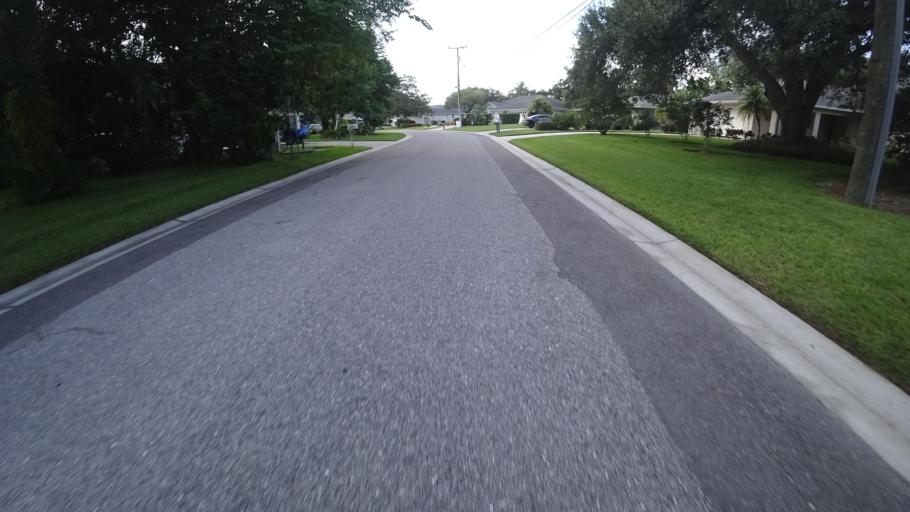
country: US
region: Florida
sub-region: Sarasota County
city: Desoto Lakes
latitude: 27.4017
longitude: -82.4954
